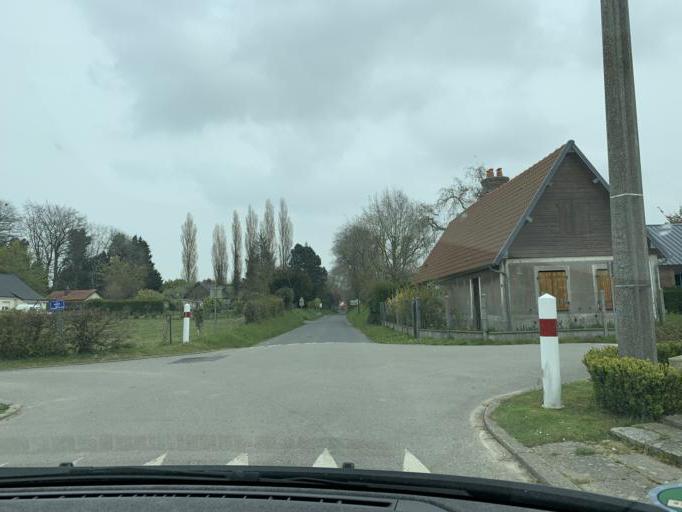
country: FR
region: Haute-Normandie
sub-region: Departement de la Seine-Maritime
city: Fontaine-le-Dun
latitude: 49.8543
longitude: 0.7995
